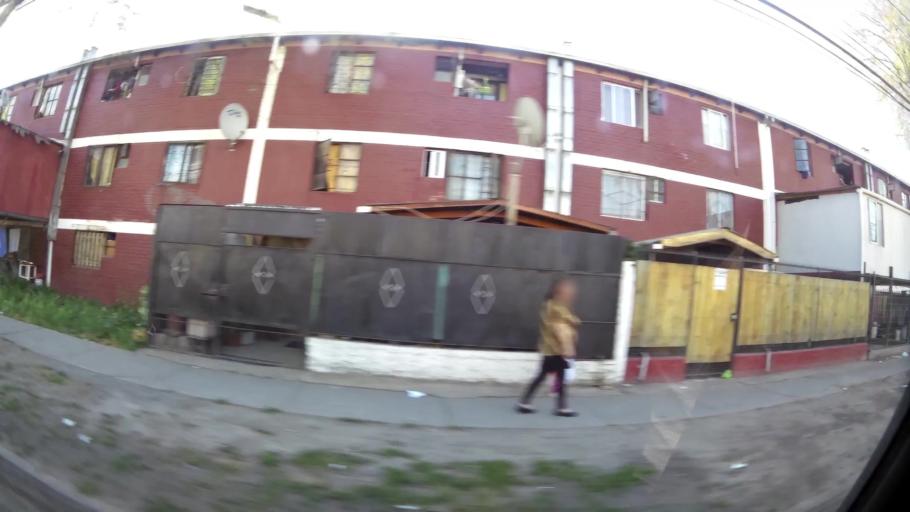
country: CL
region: Santiago Metropolitan
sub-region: Provincia de Talagante
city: Penaflor
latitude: -33.6056
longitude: -70.8608
